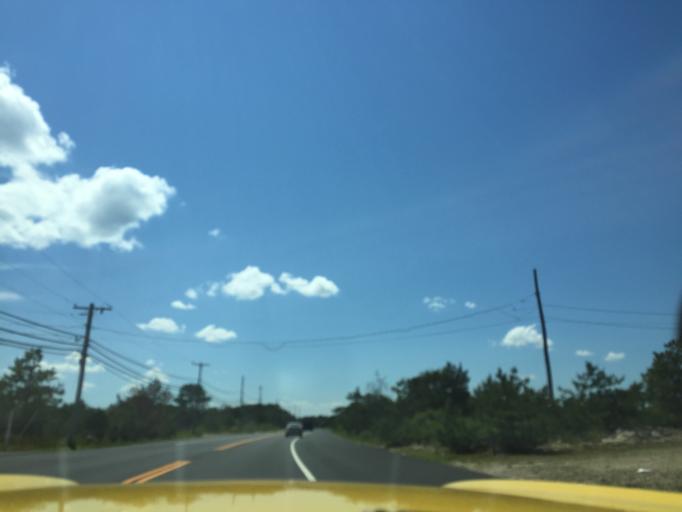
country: US
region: New York
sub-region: Suffolk County
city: Amagansett
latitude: 40.9953
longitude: -72.0559
